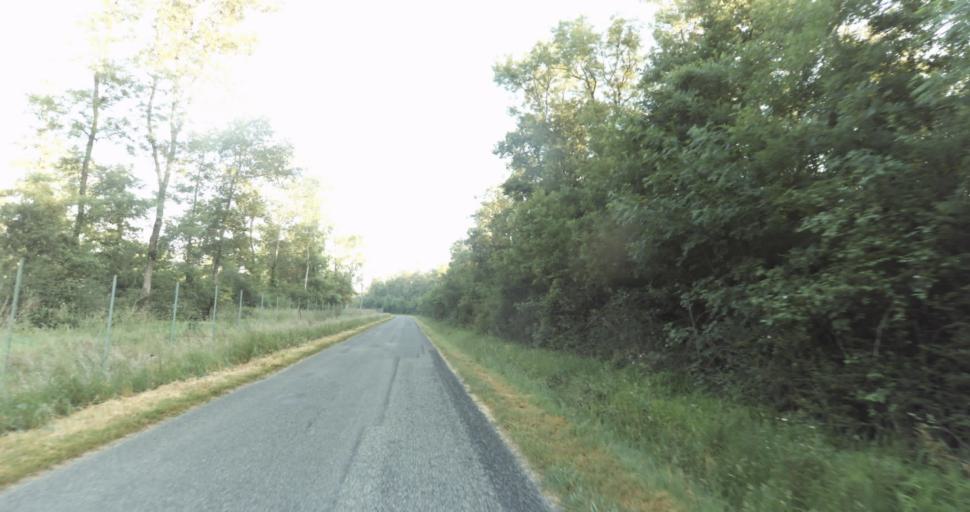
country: FR
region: Midi-Pyrenees
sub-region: Departement de la Haute-Garonne
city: Fontenilles
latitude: 43.5689
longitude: 1.1927
